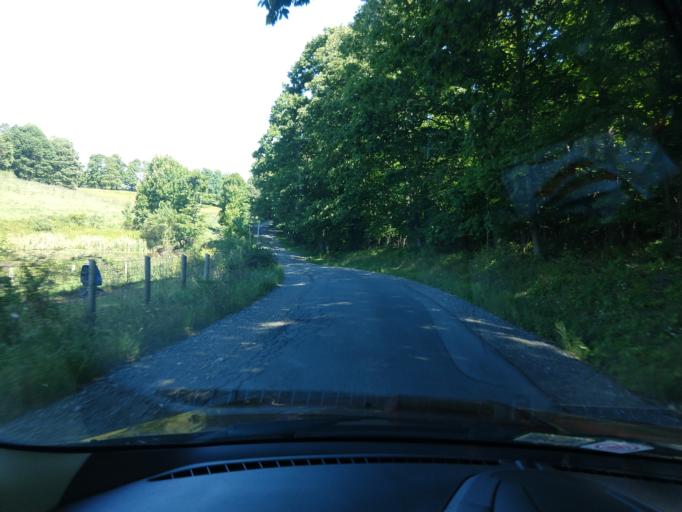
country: US
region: West Virginia
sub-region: Nicholas County
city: Craigsville
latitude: 38.2396
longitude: -80.7089
